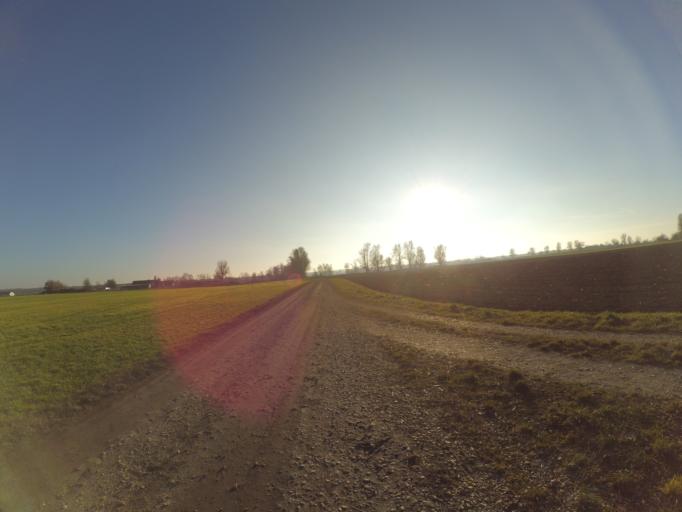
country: DE
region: Bavaria
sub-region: Swabia
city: Leipheim
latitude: 48.4721
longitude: 10.2083
